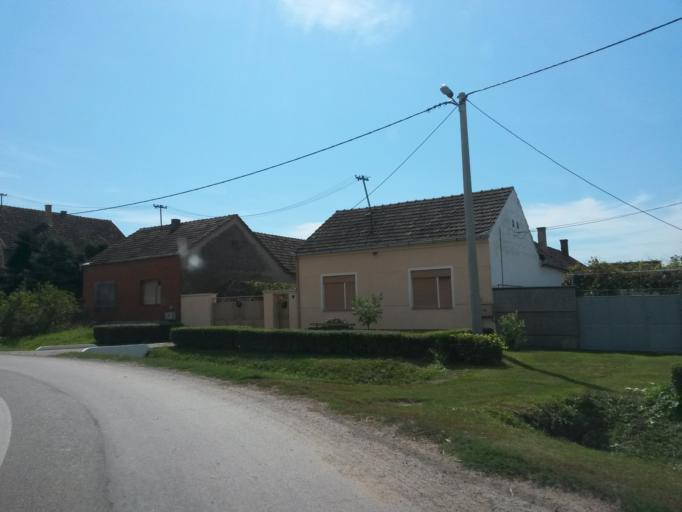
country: HR
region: Vukovarsko-Srijemska
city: Vinkovci
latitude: 45.3406
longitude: 18.7842
